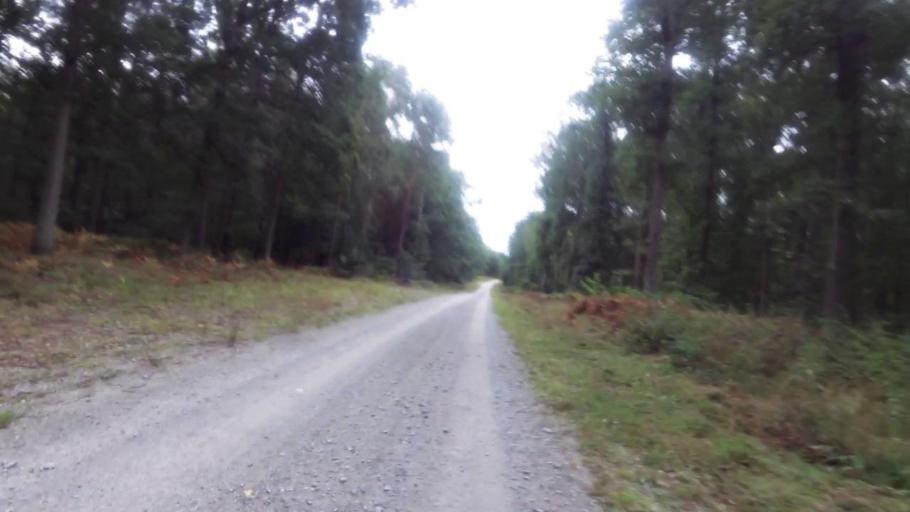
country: PL
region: Lubusz
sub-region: Powiat gorzowski
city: Kostrzyn nad Odra
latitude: 52.6402
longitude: 14.6441
